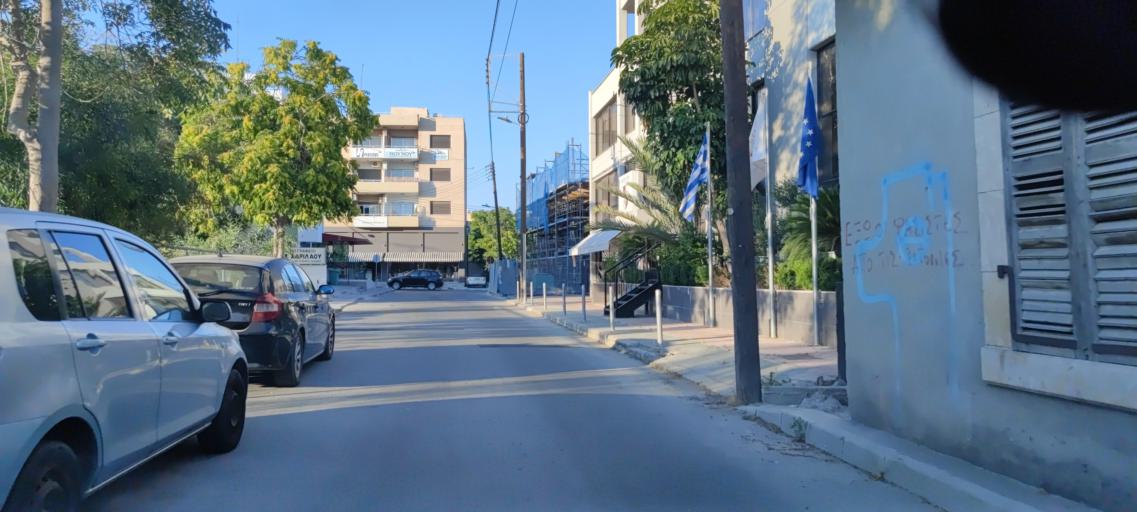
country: CY
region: Limassol
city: Limassol
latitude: 34.6768
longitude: 33.0380
